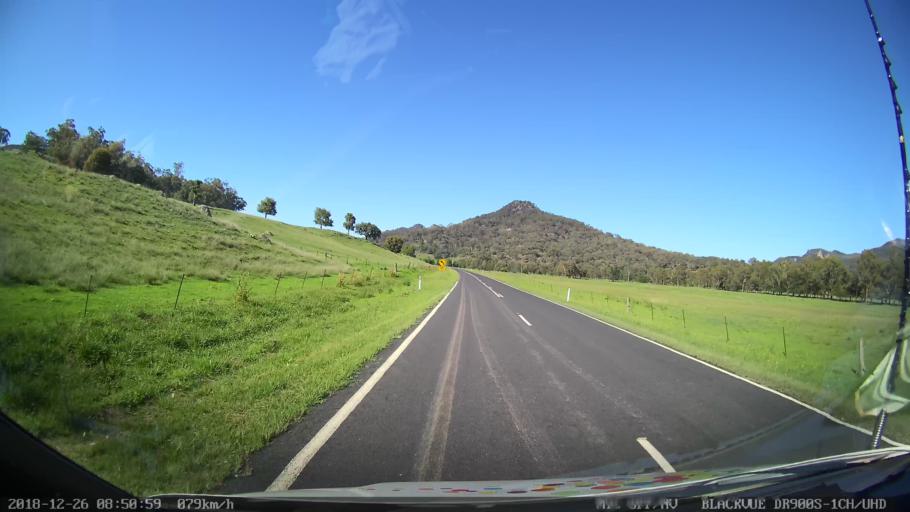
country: AU
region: New South Wales
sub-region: Mid-Western Regional
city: Kandos
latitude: -32.5813
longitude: 150.0910
